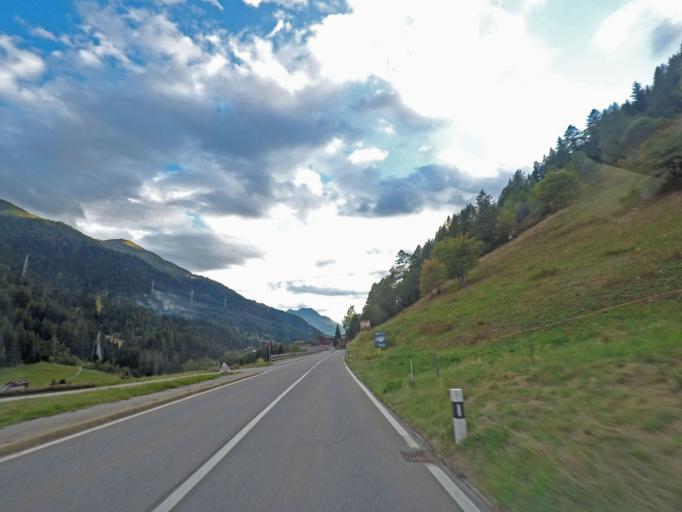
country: CH
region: Valais
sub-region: Goms District
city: Fiesch
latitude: 46.4462
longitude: 8.2061
